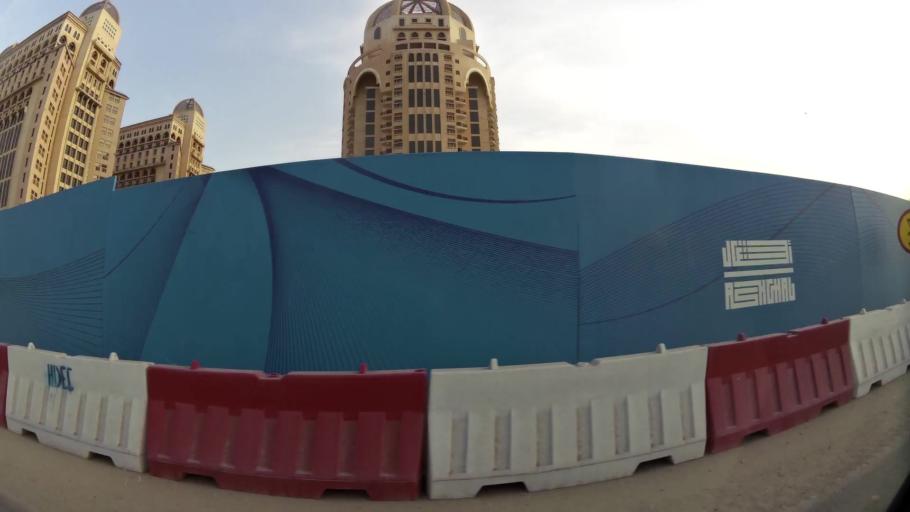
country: QA
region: Baladiyat ad Dawhah
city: Doha
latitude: 25.3515
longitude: 51.5268
